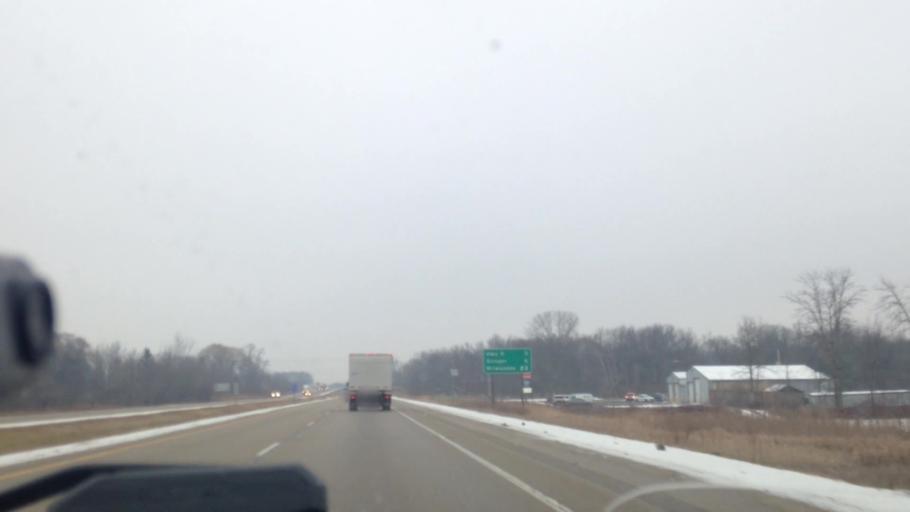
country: US
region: Wisconsin
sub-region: Washington County
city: Slinger
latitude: 43.4150
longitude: -88.3319
